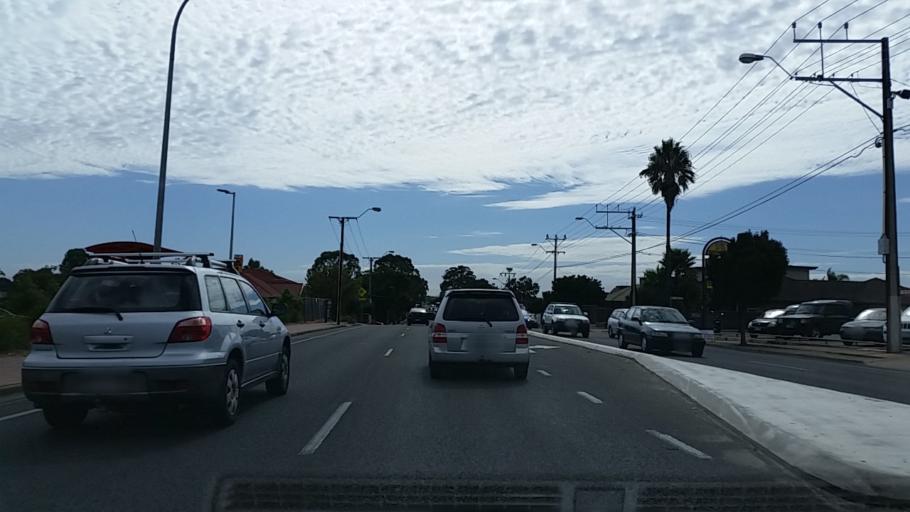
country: AU
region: South Australia
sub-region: Campbelltown
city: Hectorville
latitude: -34.8853
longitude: 138.6591
